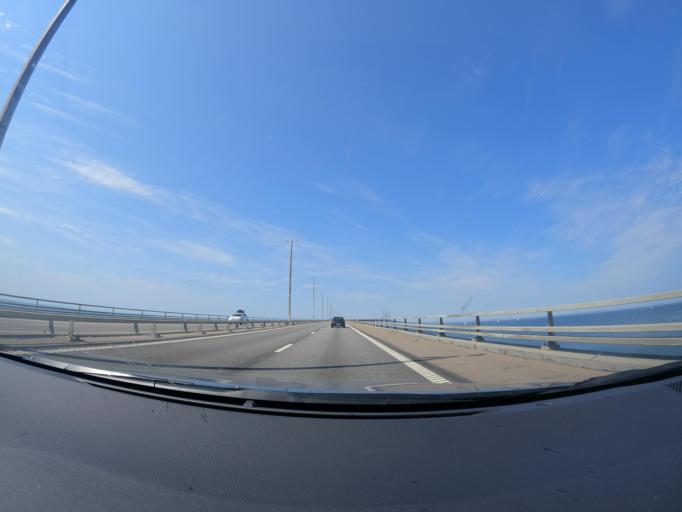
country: SE
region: Skane
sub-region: Malmo
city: Bunkeflostrand
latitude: 55.5728
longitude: 12.8768
